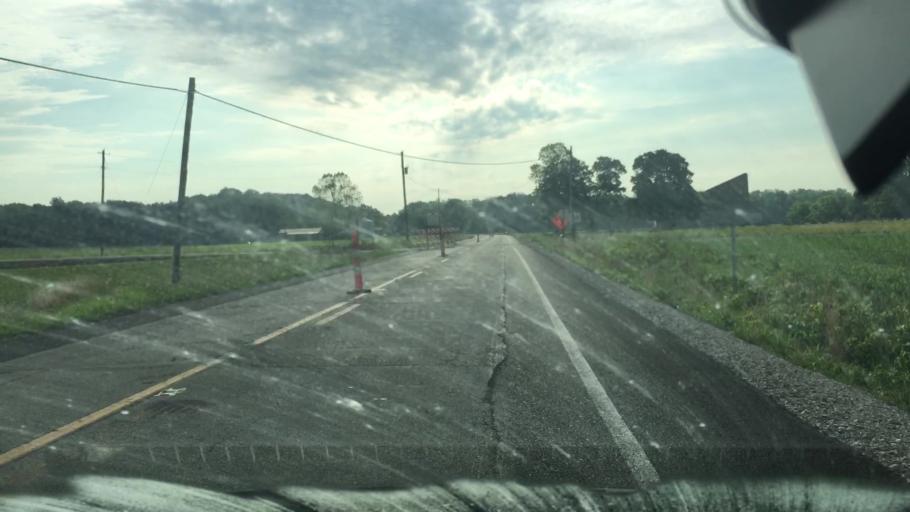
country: US
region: Kentucky
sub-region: Hancock County
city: Lewisport
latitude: 37.9507
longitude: -86.9566
